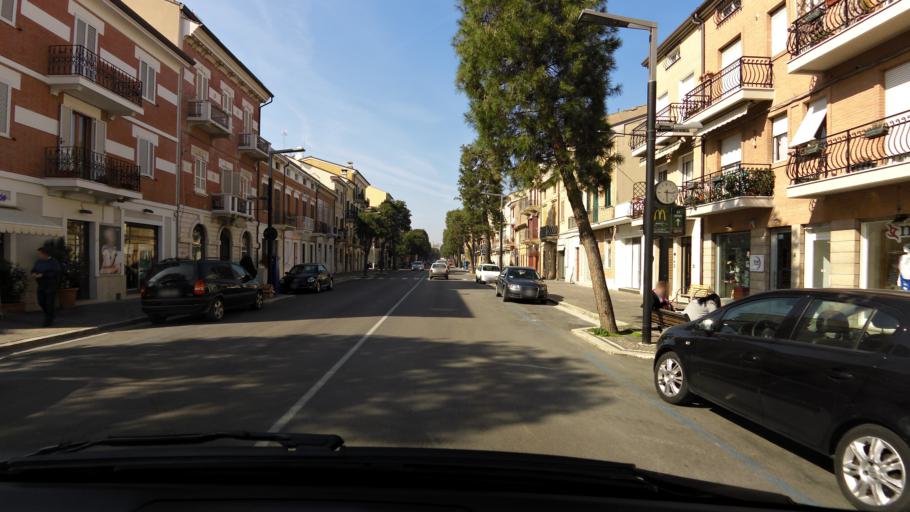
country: IT
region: The Marches
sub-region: Provincia di Macerata
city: Porto Recanati
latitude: 43.4302
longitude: 13.6649
